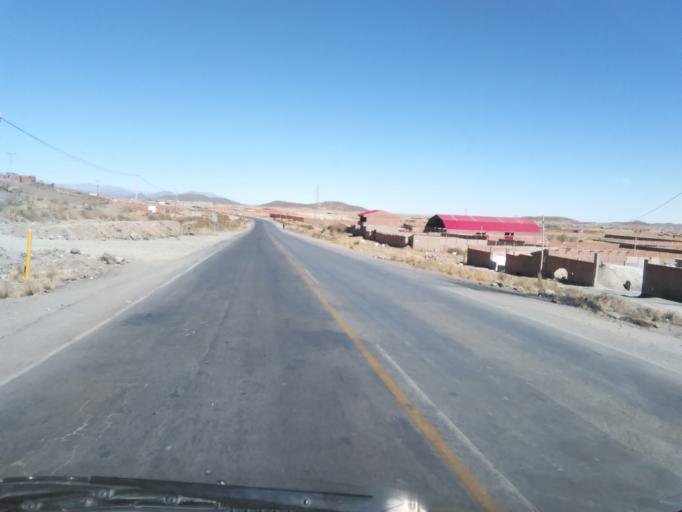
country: BO
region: Oruro
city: Oruro
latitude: -17.9853
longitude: -67.0493
